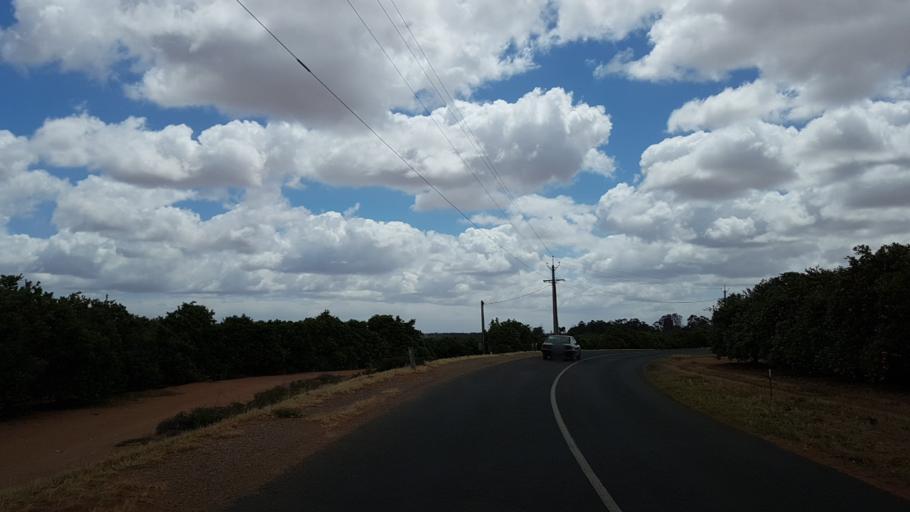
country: AU
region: South Australia
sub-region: Loxton Waikerie
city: Waikerie
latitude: -34.1766
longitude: 140.0273
